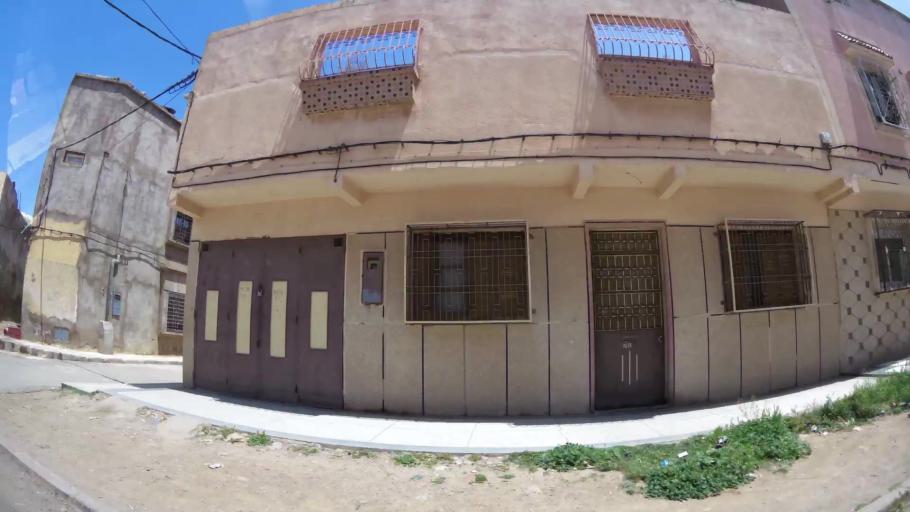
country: MA
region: Oriental
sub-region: Oujda-Angad
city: Oujda
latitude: 34.6840
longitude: -1.9004
